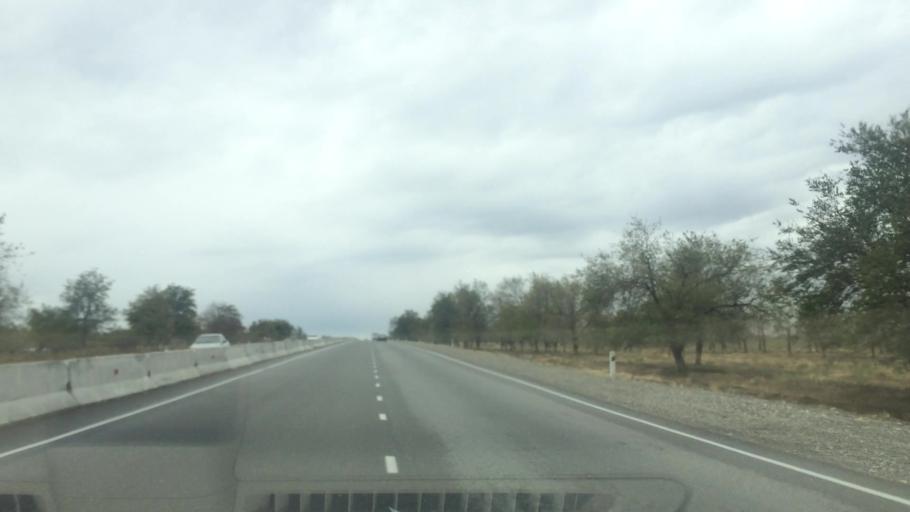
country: UZ
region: Samarqand
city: Bulung'ur
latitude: 39.9332
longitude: 67.5235
